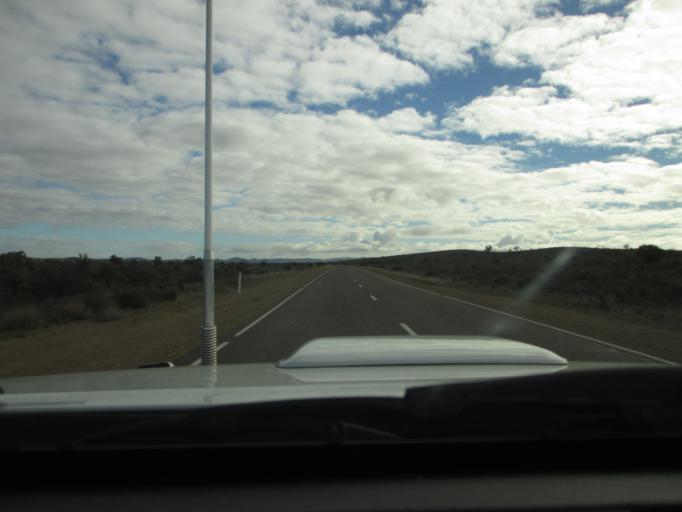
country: AU
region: South Australia
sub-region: Flinders Ranges
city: Quorn
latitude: -32.3642
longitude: 138.4965
